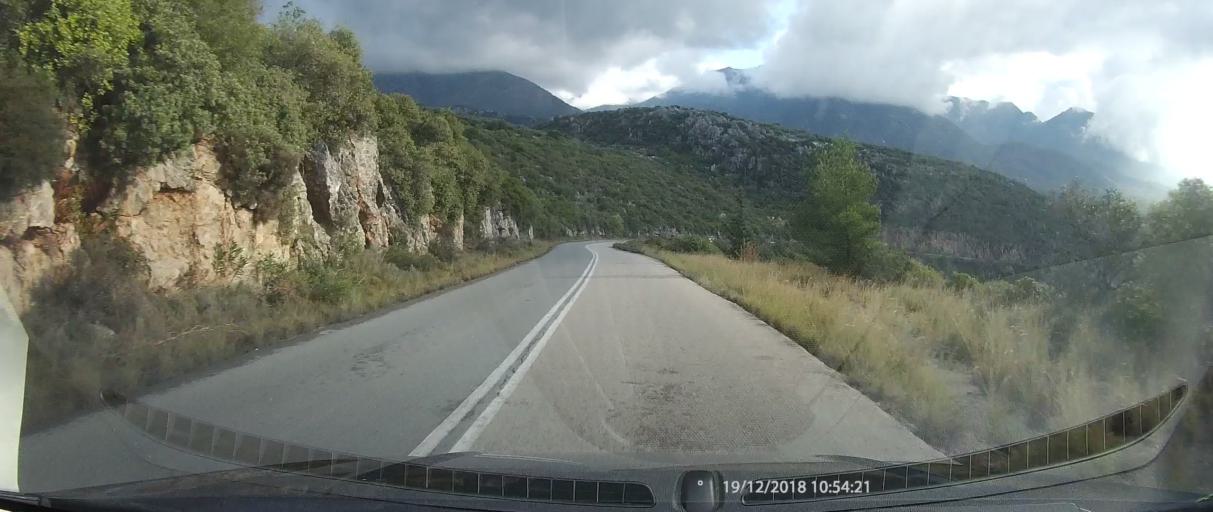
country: GR
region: Peloponnese
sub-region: Nomos Messinias
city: Kardamyli
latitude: 36.9074
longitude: 22.2313
